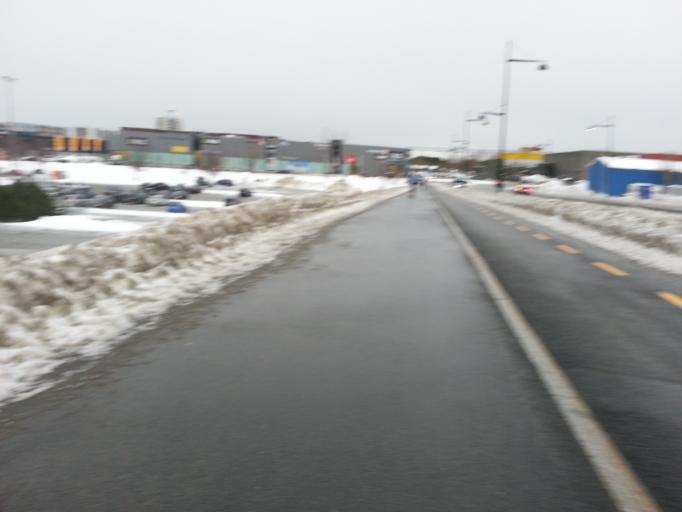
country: NO
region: Sor-Trondelag
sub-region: Trondheim
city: Trondheim
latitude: 63.4382
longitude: 10.4611
